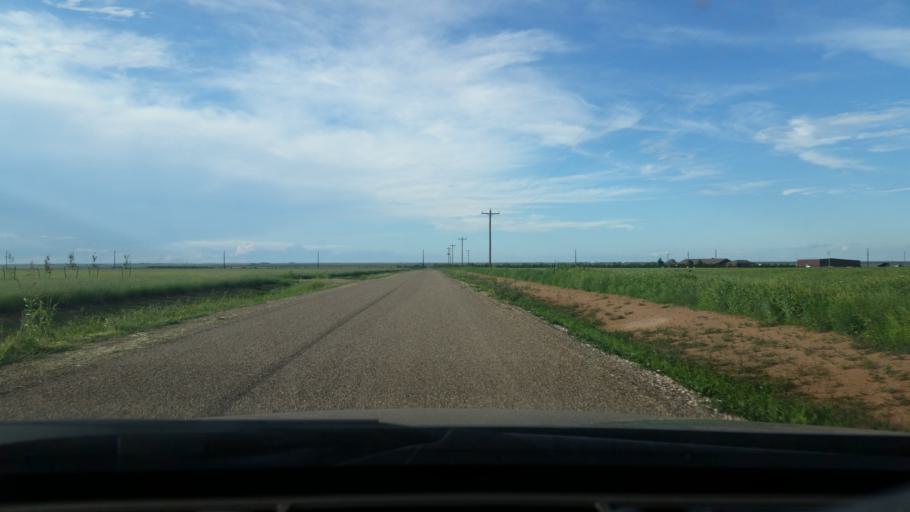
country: US
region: New Mexico
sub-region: Curry County
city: Clovis
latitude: 34.4959
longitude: -103.1788
